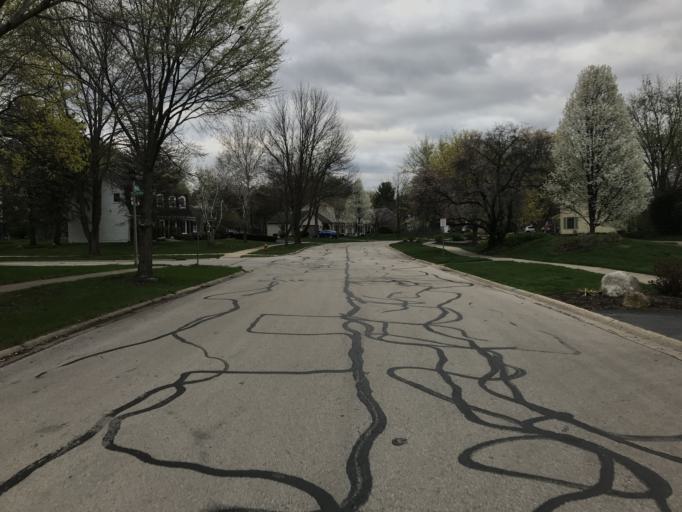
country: US
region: Illinois
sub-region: Will County
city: Bolingbrook
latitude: 41.7374
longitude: -88.1128
